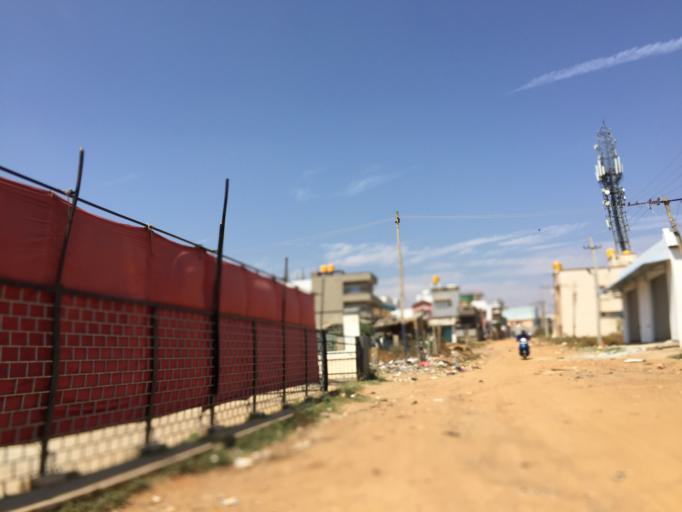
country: IN
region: Karnataka
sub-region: Kolar
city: Kolar
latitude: 13.1285
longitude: 78.1174
